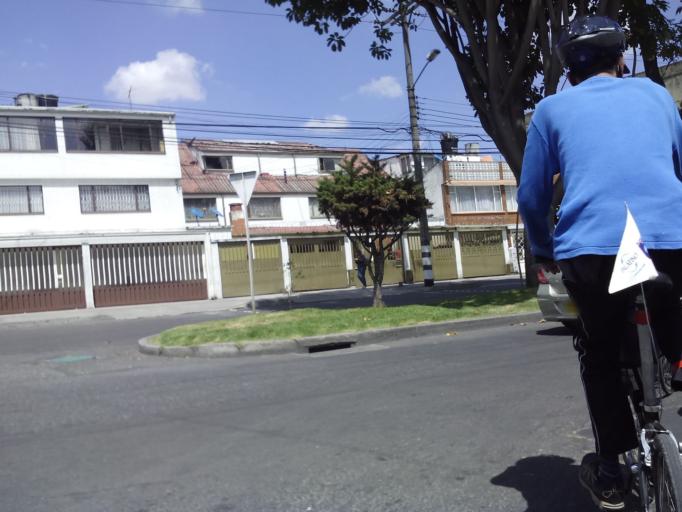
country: CO
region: Cundinamarca
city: Funza
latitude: 4.6790
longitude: -74.1339
